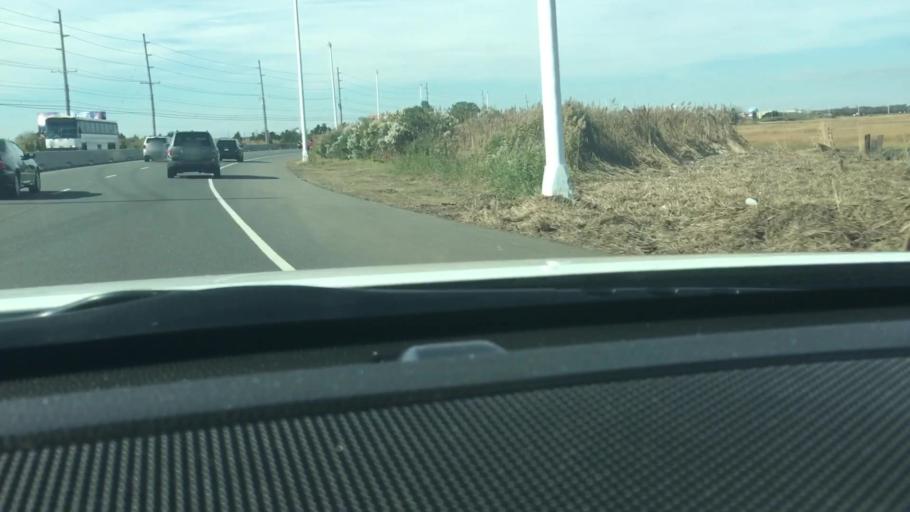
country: US
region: New Jersey
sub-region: Atlantic County
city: Pleasantville
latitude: 39.3900
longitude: -74.4859
